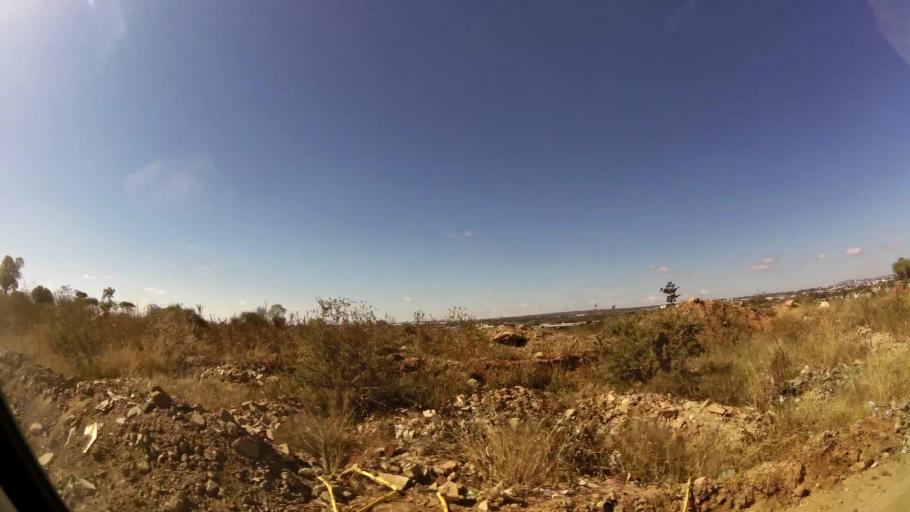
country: ZA
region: Limpopo
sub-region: Capricorn District Municipality
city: Polokwane
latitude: -23.8753
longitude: 29.4251
